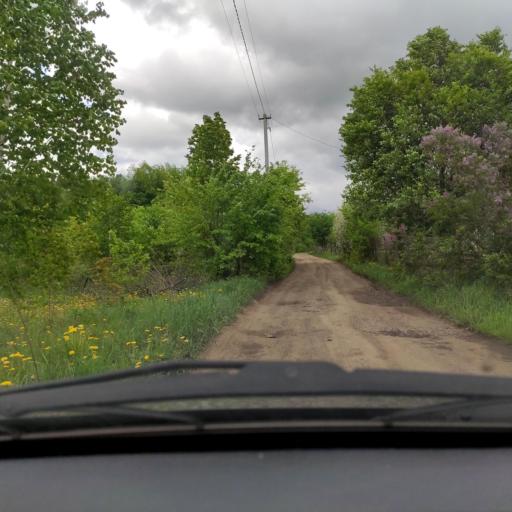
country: RU
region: Bashkortostan
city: Kabakovo
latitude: 54.7070
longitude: 56.1601
